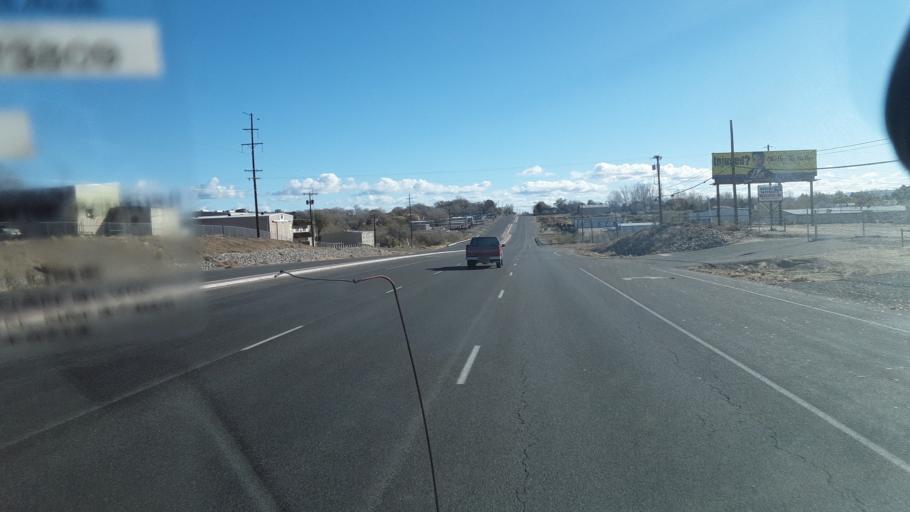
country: US
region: New Mexico
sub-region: San Juan County
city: Lee Acres
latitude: 36.7010
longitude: -108.0672
